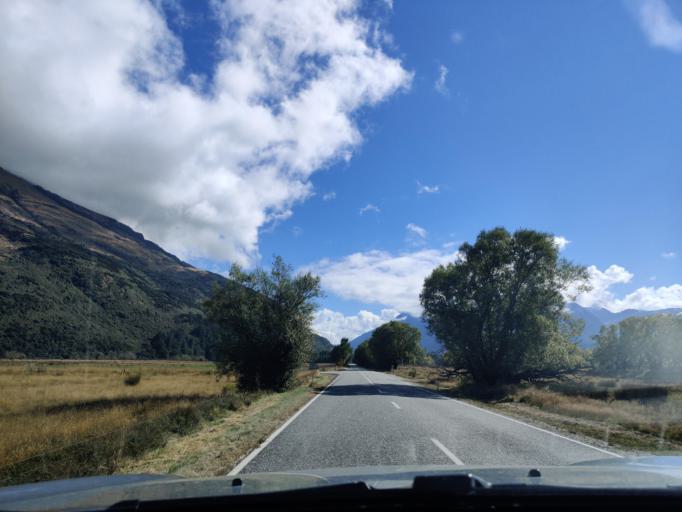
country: NZ
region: Otago
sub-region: Queenstown-Lakes District
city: Queenstown
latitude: -44.7839
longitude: 168.3947
